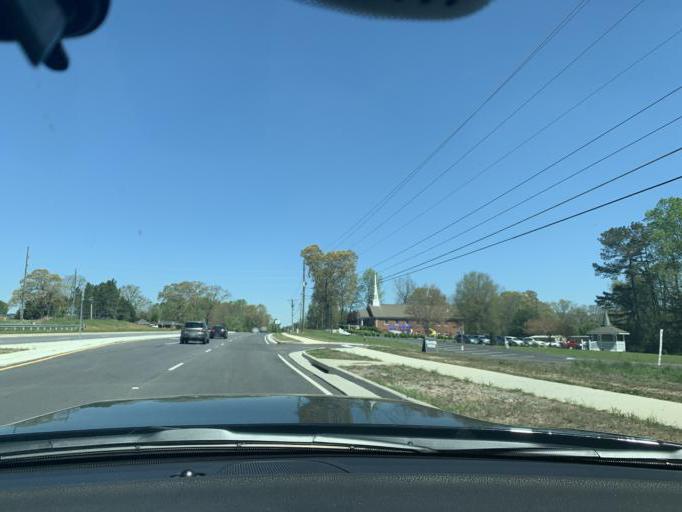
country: US
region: Georgia
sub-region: Forsyth County
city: Cumming
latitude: 34.1953
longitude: -84.1970
